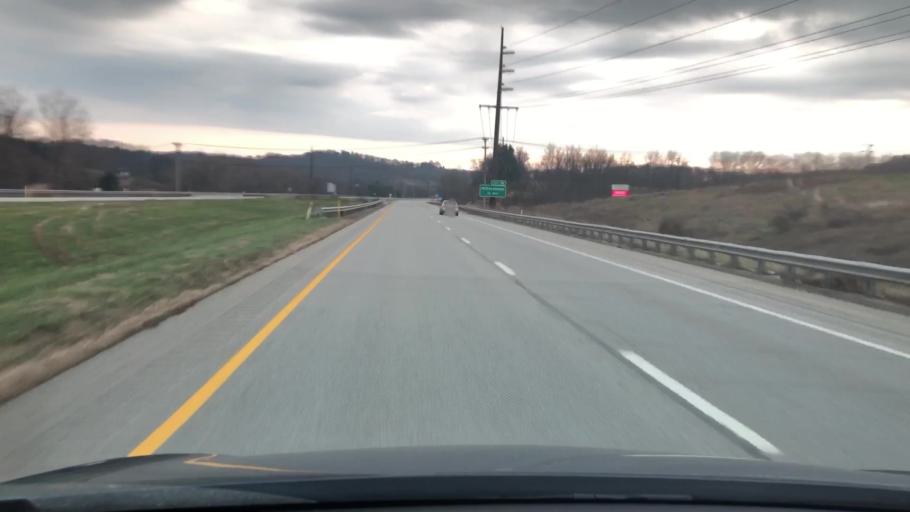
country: US
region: Pennsylvania
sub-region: Armstrong County
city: Freeport
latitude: 40.6776
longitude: -79.7143
